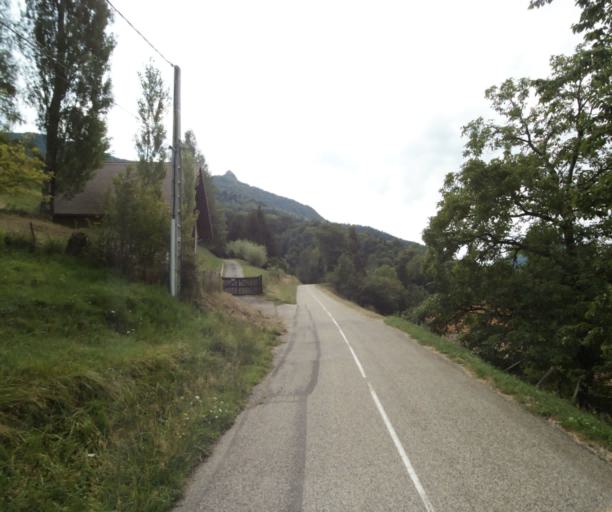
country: FR
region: Rhone-Alpes
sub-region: Departement de l'Isere
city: Saint-Egreve
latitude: 45.2757
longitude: 5.7076
